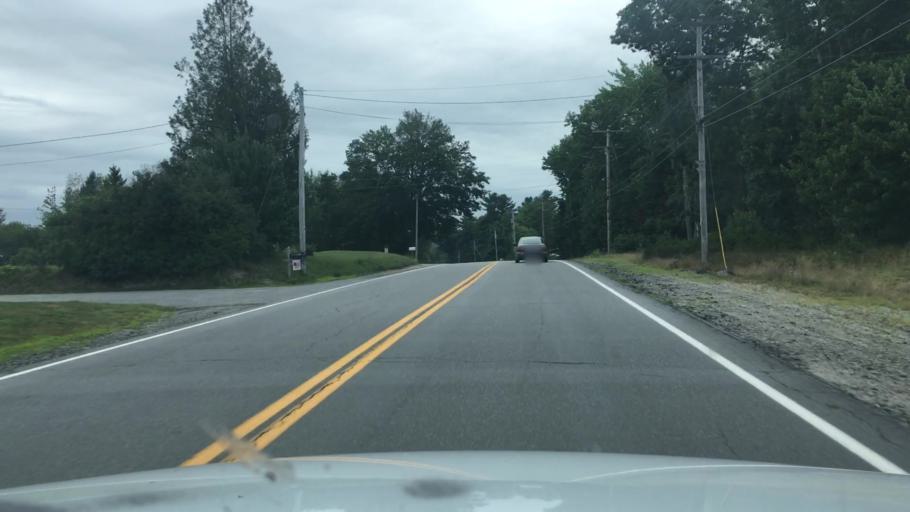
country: US
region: Maine
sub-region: Washington County
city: Cherryfield
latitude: 44.6040
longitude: -67.9425
